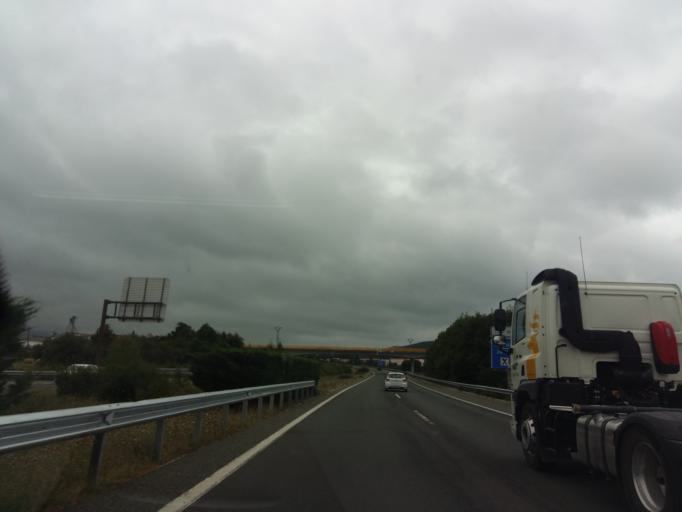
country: ES
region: Navarre
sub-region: Provincia de Navarra
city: Echarri-Aranaz
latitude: 42.8994
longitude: -2.0635
